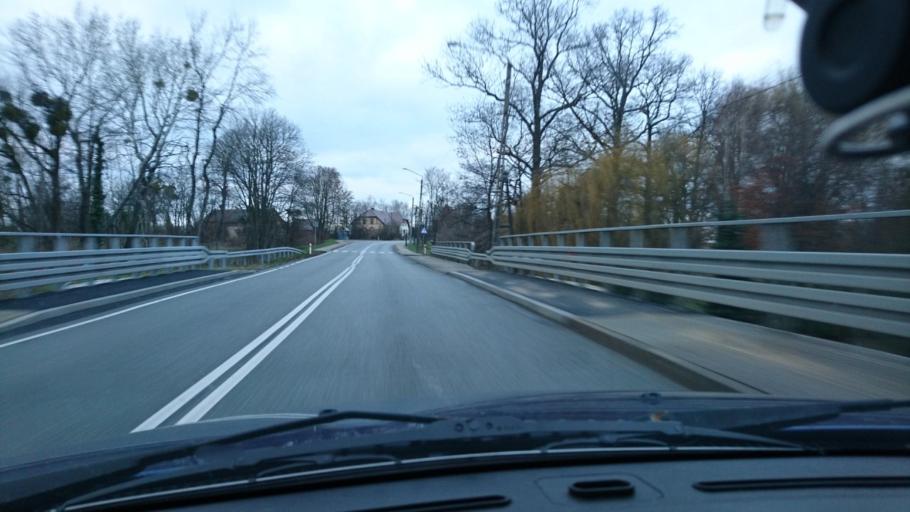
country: PL
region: Opole Voivodeship
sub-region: Powiat kluczborski
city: Byczyna
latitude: 51.0625
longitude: 18.2009
